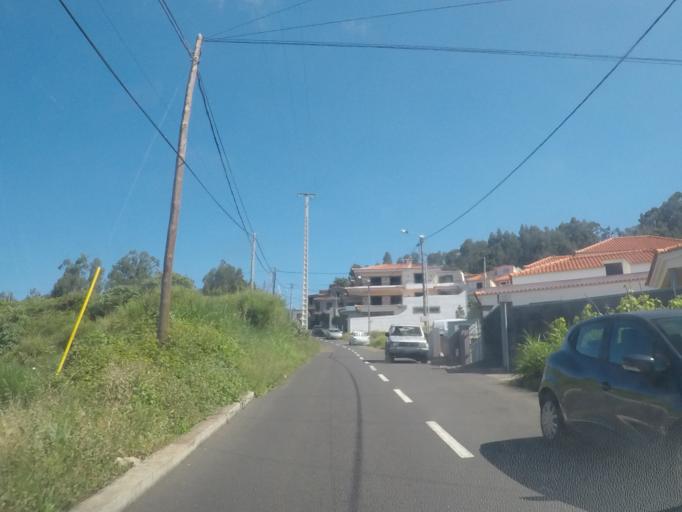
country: PT
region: Madeira
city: Camara de Lobos
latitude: 32.6757
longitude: -16.9650
